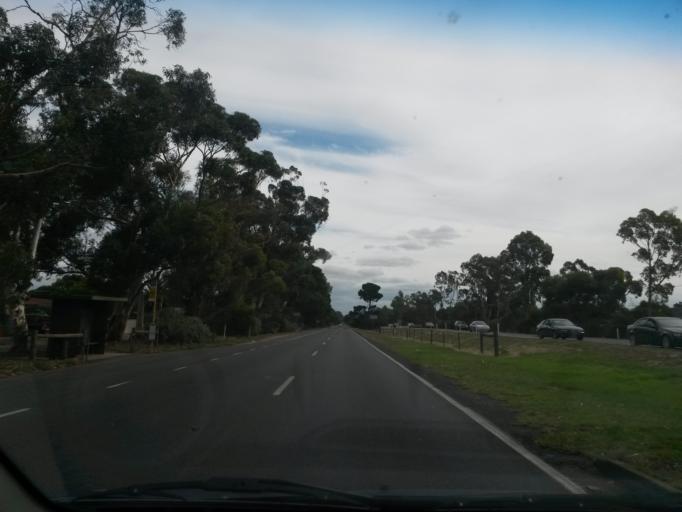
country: AU
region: South Australia
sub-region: Salisbury
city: Salisbury
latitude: -34.7751
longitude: 138.6616
